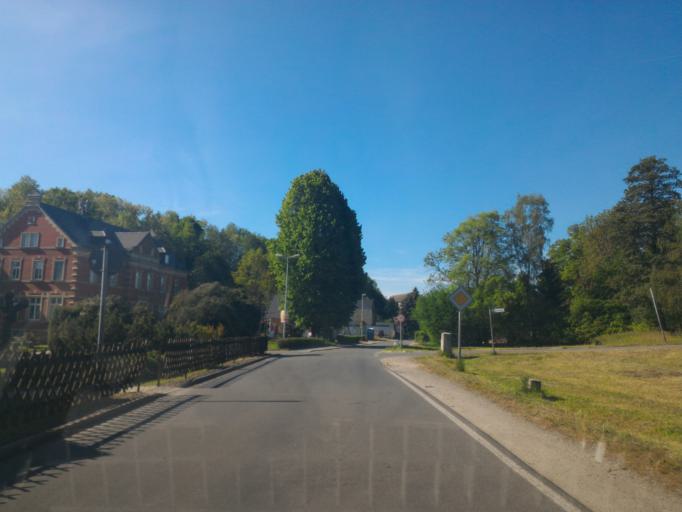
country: DE
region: Saxony
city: Grossschweidnitz
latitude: 51.0663
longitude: 14.6387
